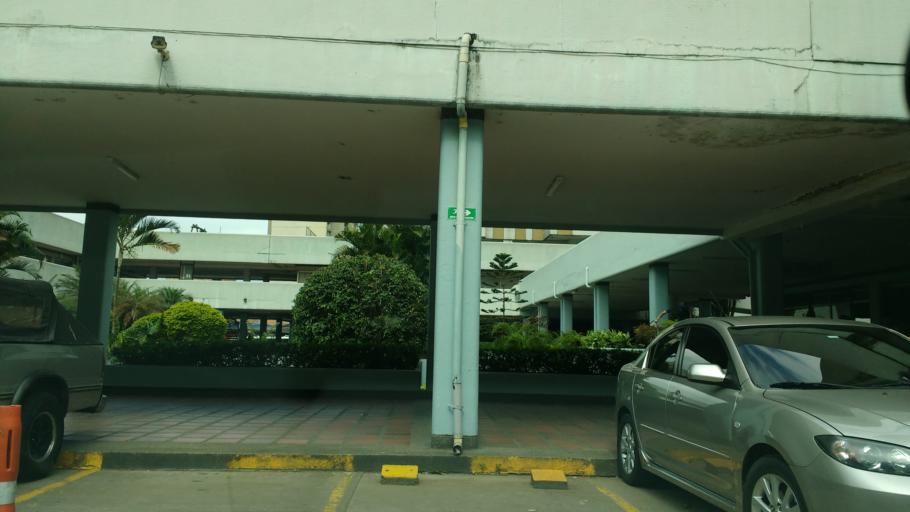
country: CO
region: Antioquia
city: Medellin
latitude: 6.2446
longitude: -75.5632
